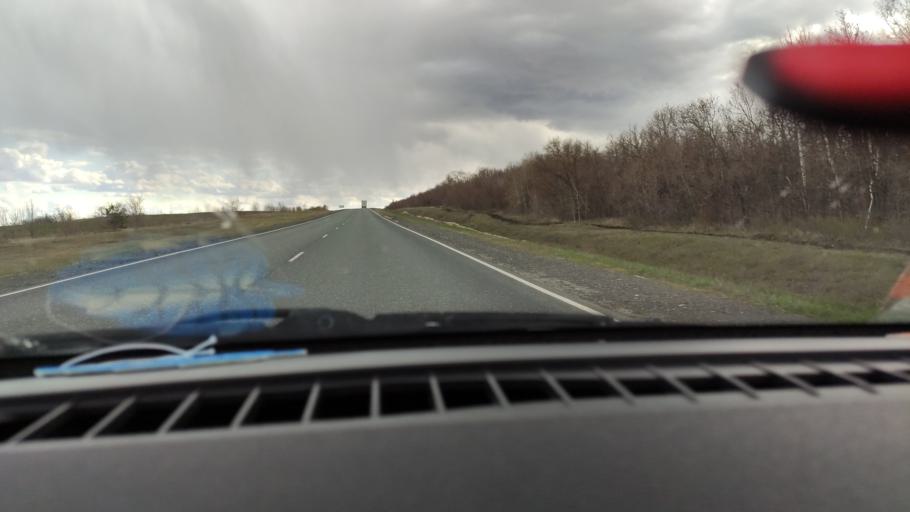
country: RU
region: Saratov
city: Balakovo
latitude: 52.1827
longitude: 47.8439
